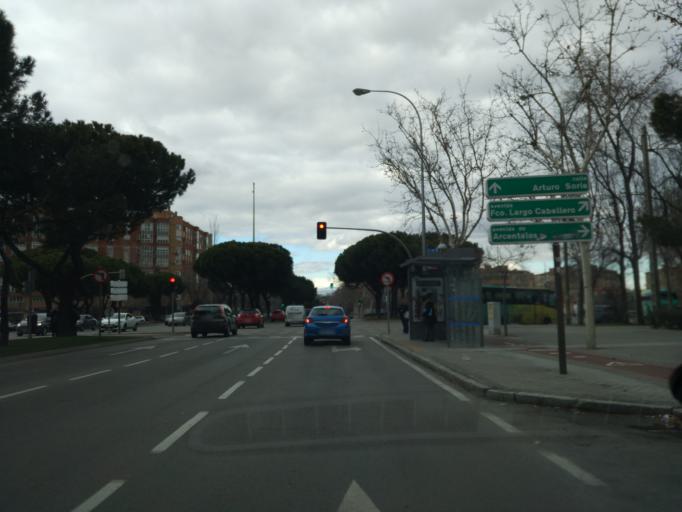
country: ES
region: Madrid
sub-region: Provincia de Madrid
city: San Blas
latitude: 40.4239
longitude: -3.6277
